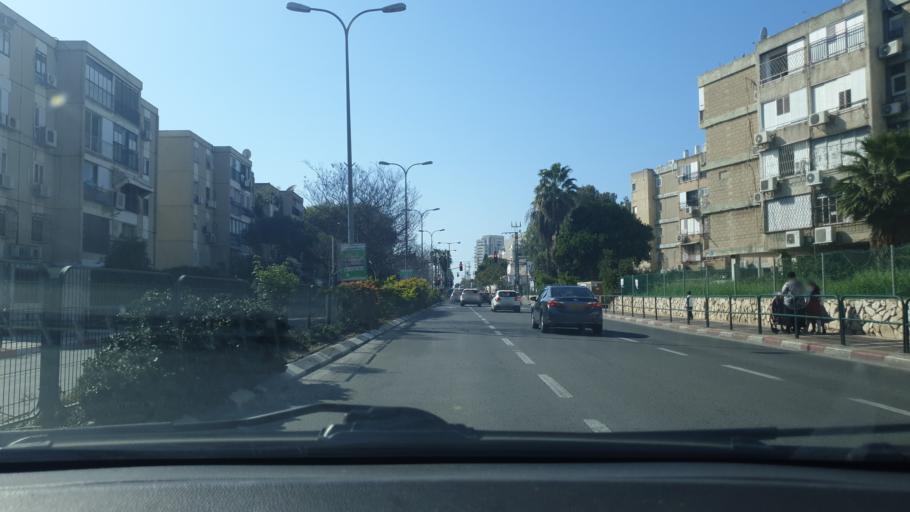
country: IL
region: Tel Aviv
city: Azor
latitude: 32.0453
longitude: 34.8075
